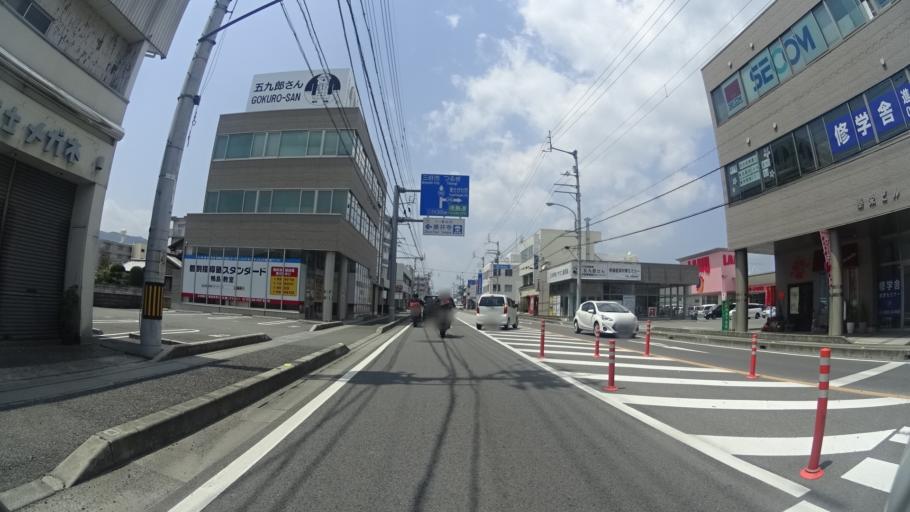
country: JP
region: Tokushima
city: Kamojimacho-jogejima
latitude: 34.0682
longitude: 134.3542
